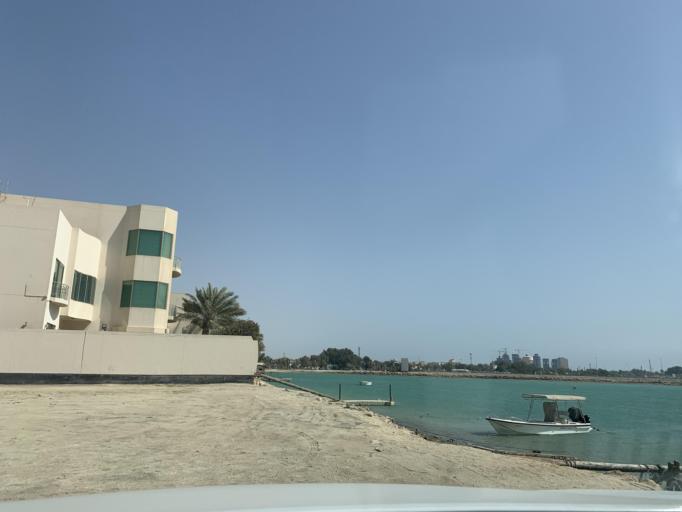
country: BH
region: Manama
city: Jidd Hafs
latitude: 26.2288
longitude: 50.4602
